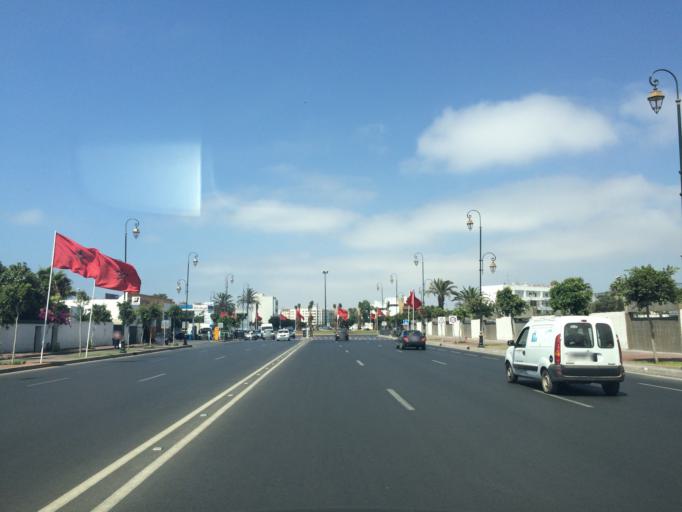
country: MA
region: Rabat-Sale-Zemmour-Zaer
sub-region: Rabat
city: Rabat
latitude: 34.0073
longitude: -6.8553
